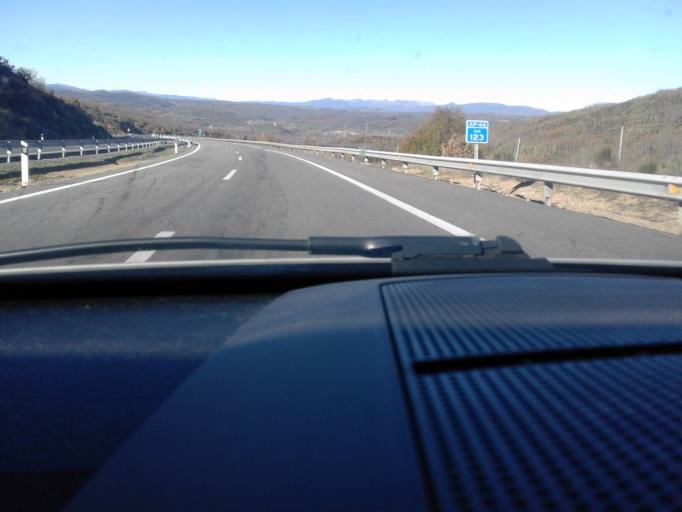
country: ES
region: Castille and Leon
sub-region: Provincia de Leon
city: Santa Maria de Ordas
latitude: 42.7041
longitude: -5.7837
